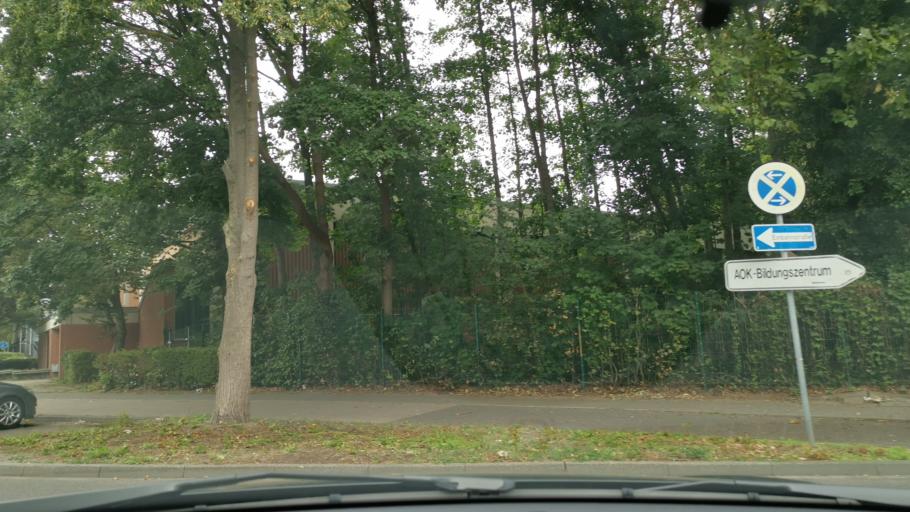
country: DE
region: North Rhine-Westphalia
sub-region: Regierungsbezirk Dusseldorf
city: Grevenbroich
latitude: 51.0845
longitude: 6.5794
